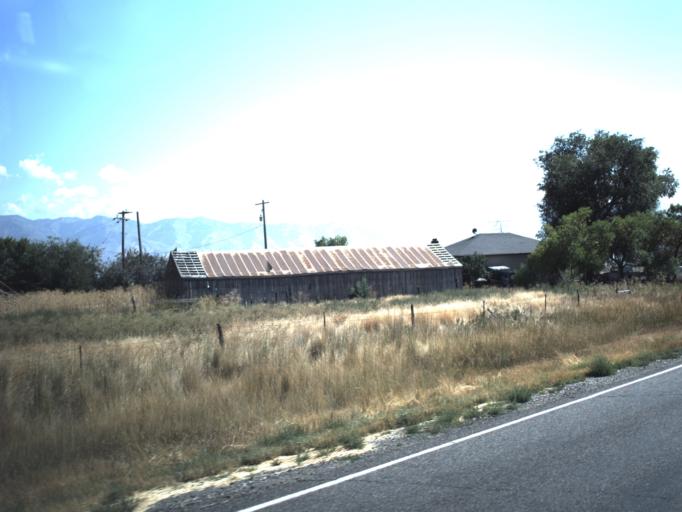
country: US
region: Utah
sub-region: Cache County
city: Benson
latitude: 41.8468
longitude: -111.9668
